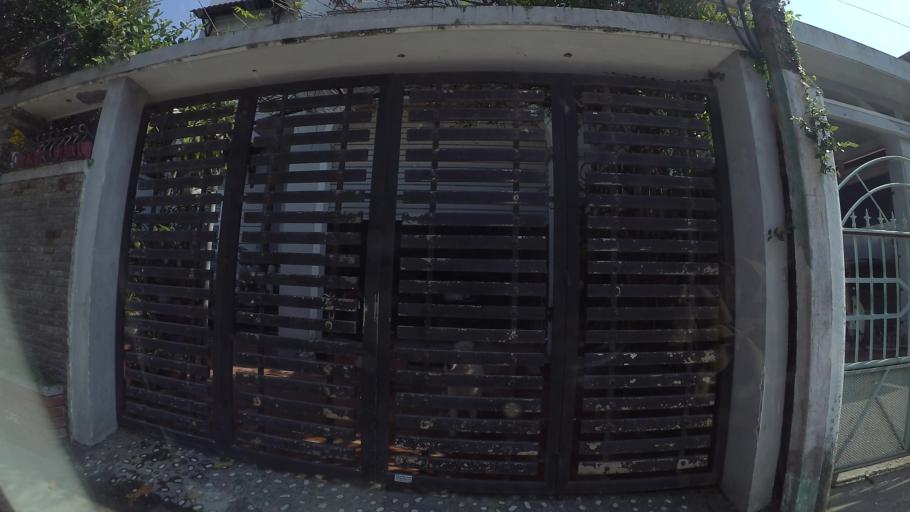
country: VN
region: Da Nang
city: Ngu Hanh Son
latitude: 16.0389
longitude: 108.2483
